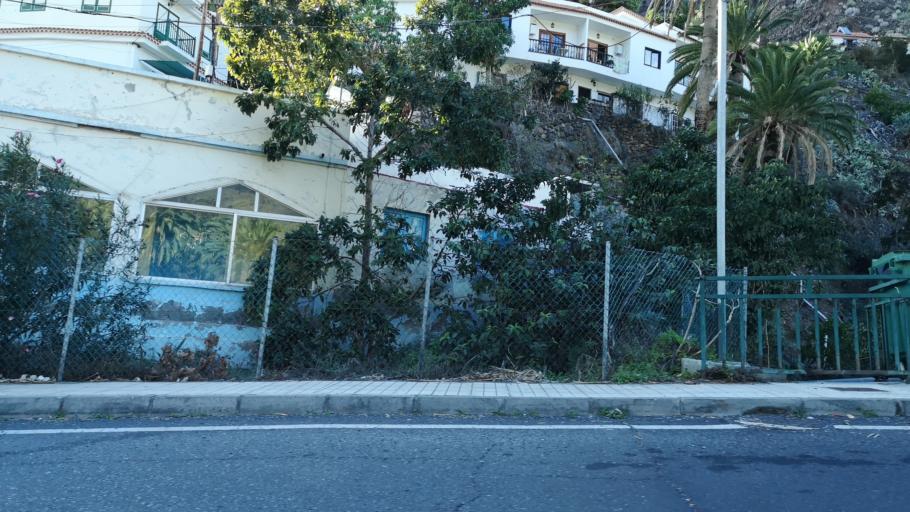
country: ES
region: Canary Islands
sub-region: Provincia de Santa Cruz de Tenerife
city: Vallehermosa
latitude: 28.1064
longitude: -17.3261
